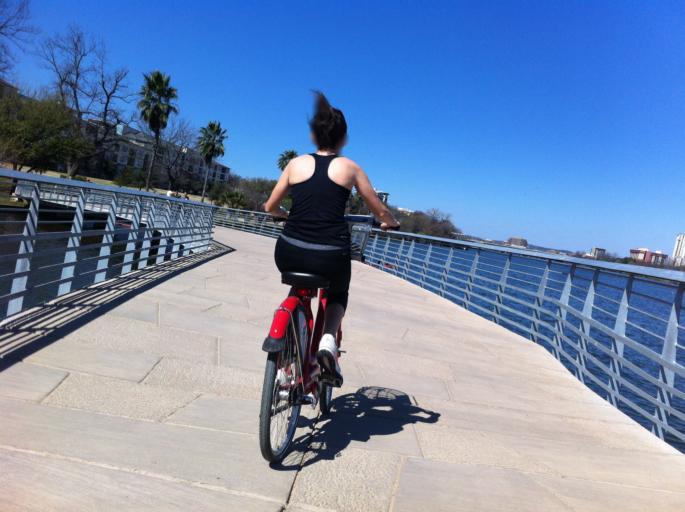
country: US
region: Texas
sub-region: Travis County
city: Austin
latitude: 30.2454
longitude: -97.7256
